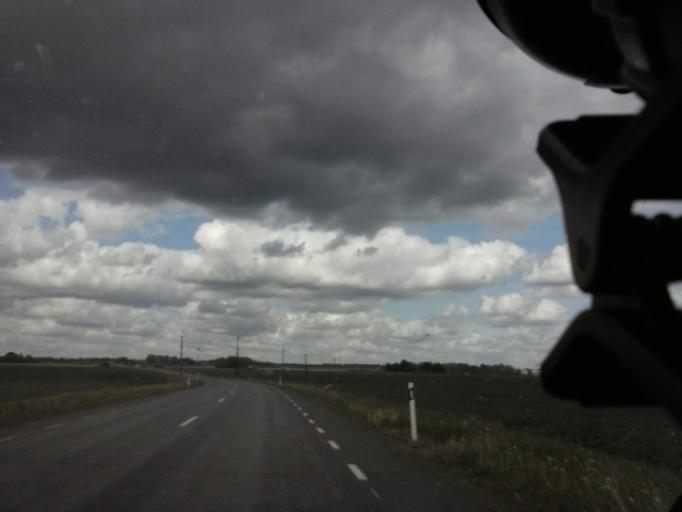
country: EE
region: Jogevamaa
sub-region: Poltsamaa linn
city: Poltsamaa
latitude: 58.6434
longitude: 25.9198
